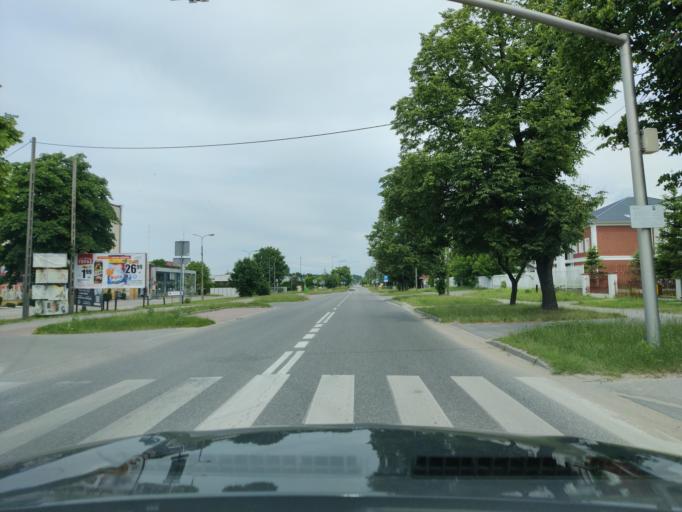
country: PL
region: Masovian Voivodeship
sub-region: Powiat wyszkowski
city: Wyszkow
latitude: 52.6059
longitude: 21.4551
